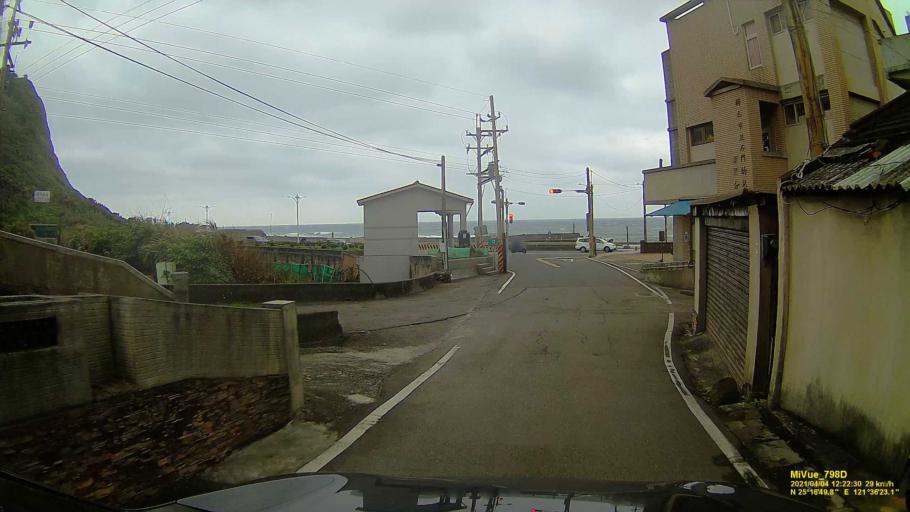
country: TW
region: Taiwan
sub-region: Keelung
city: Keelung
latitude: 25.2807
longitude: 121.6065
